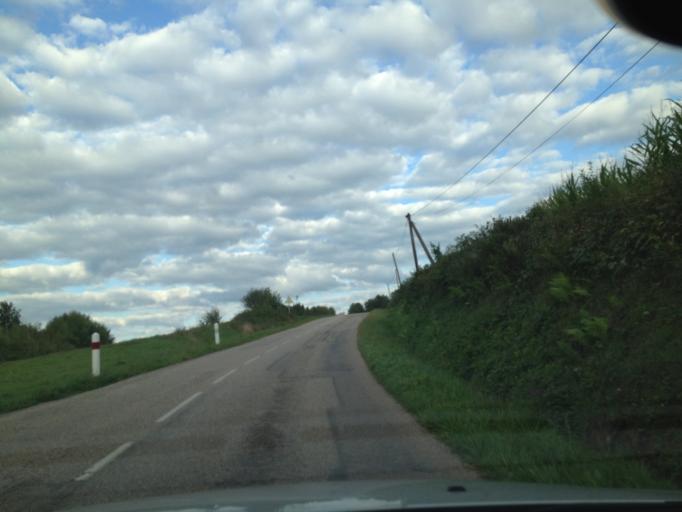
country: FR
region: Lorraine
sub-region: Departement des Vosges
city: Bains-les-Bains
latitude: 47.9769
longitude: 6.1667
